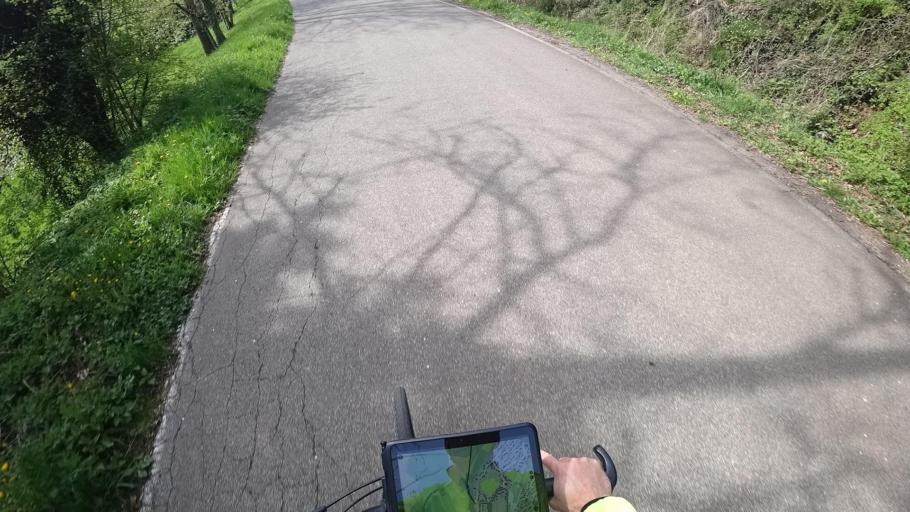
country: DE
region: Rheinland-Pfalz
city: Newel
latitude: 49.8137
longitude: 6.6116
